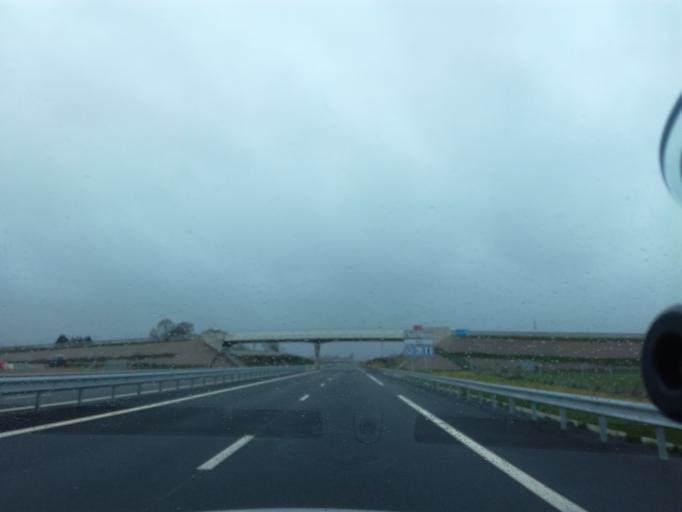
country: FR
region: Brittany
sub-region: Departement d'Ille-et-Vilaine
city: Boisgervilly
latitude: 48.1976
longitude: -2.0898
